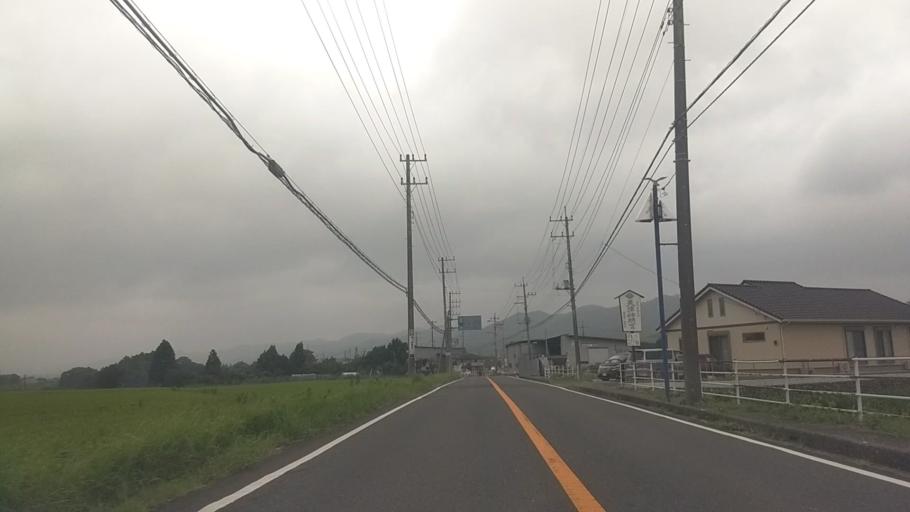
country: JP
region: Chiba
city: Kawaguchi
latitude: 35.1241
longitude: 140.0604
